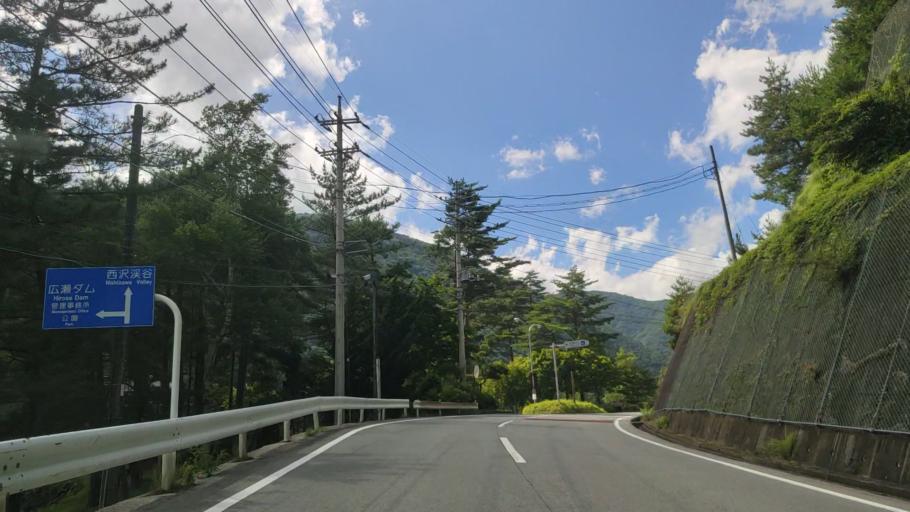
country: JP
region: Yamanashi
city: Enzan
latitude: 35.8400
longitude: 138.7649
